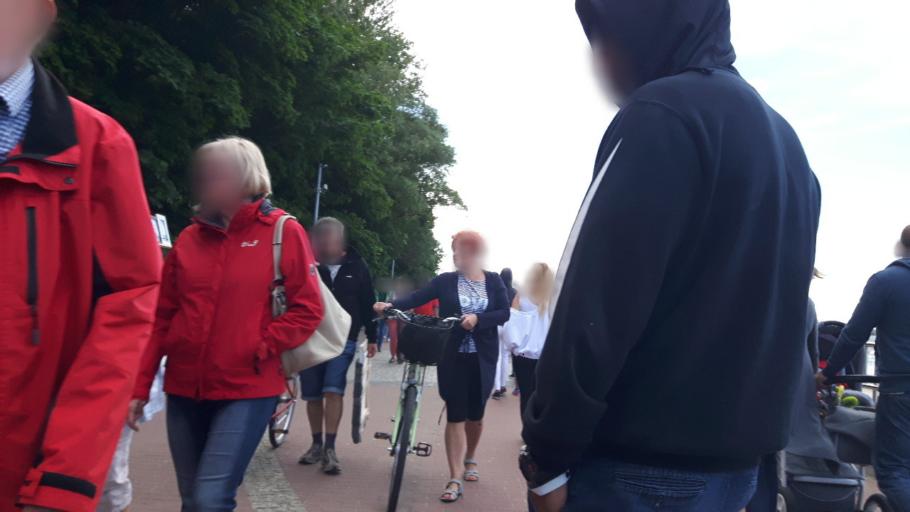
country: PL
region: West Pomeranian Voivodeship
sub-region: Powiat kolobrzeski
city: Kolobrzeg
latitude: 54.1864
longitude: 15.5599
